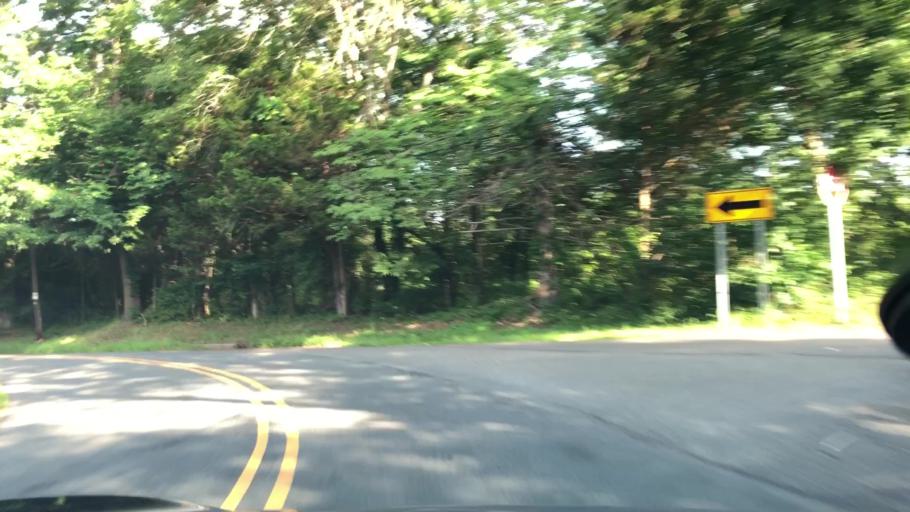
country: US
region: New Jersey
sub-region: Mercer County
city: Pennington
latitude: 40.3516
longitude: -74.7762
